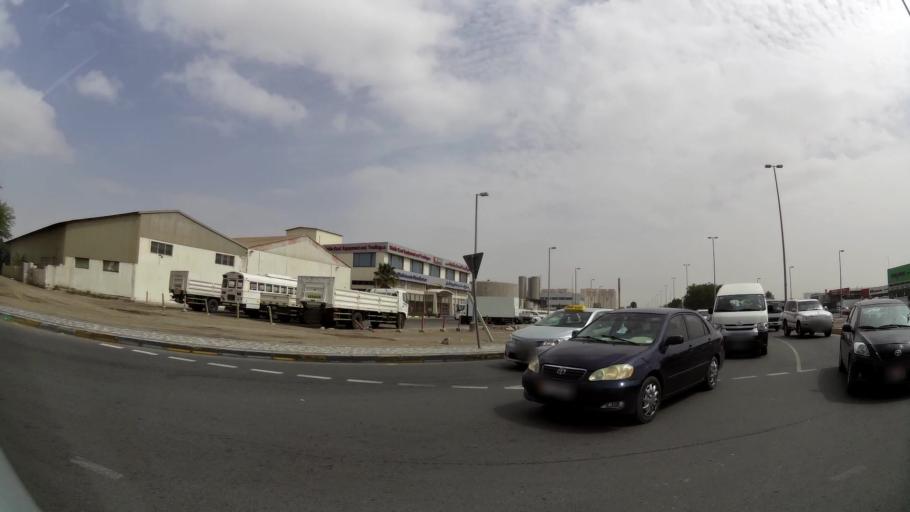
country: AE
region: Abu Dhabi
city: Abu Dhabi
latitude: 24.3825
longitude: 54.5109
